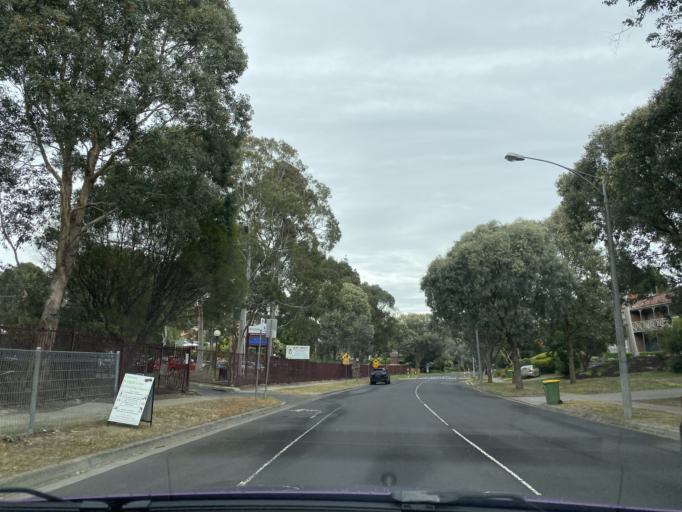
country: AU
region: Victoria
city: Saint Helena
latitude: -37.6976
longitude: 145.1357
